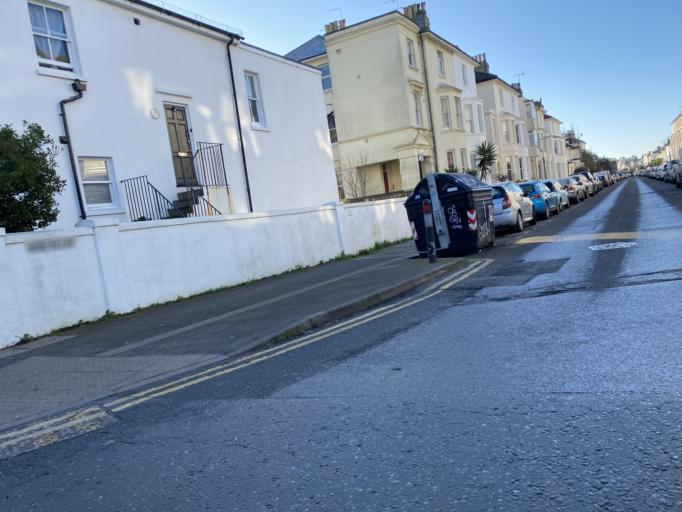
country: GB
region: England
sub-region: Brighton and Hove
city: Hove
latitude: 50.8307
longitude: -0.1712
